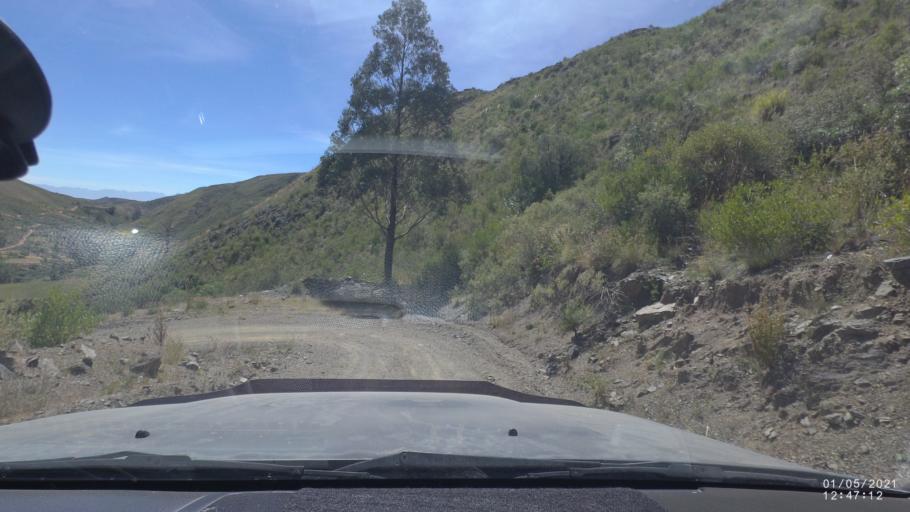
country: BO
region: Cochabamba
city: Capinota
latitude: -17.6860
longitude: -66.1609
